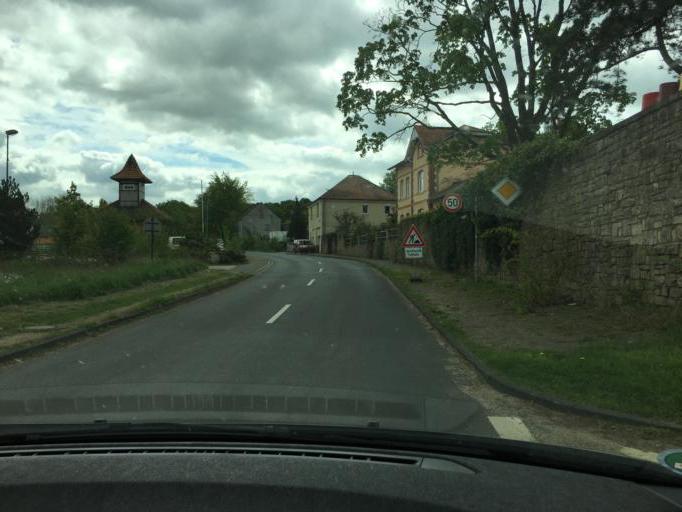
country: DE
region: North Rhine-Westphalia
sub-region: Regierungsbezirk Koln
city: Mechernich
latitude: 50.6266
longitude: 6.6928
